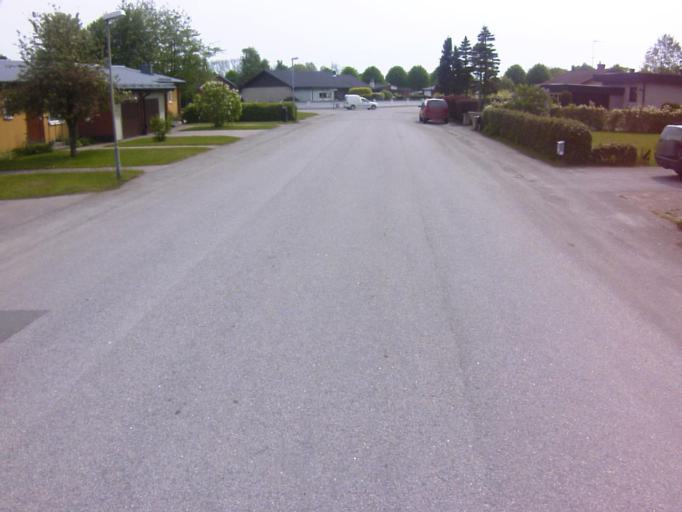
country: SE
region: Blekinge
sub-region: Solvesborgs Kommun
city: Soelvesborg
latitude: 56.0479
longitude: 14.6844
